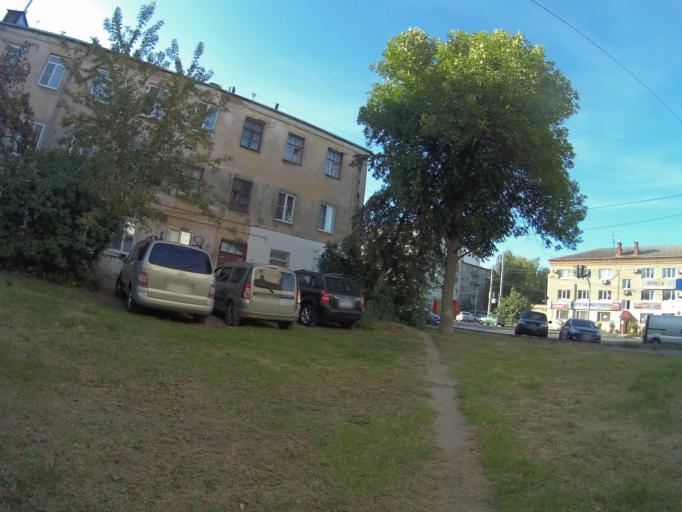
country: RU
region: Vladimir
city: Vladimir
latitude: 56.1503
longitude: 40.3786
